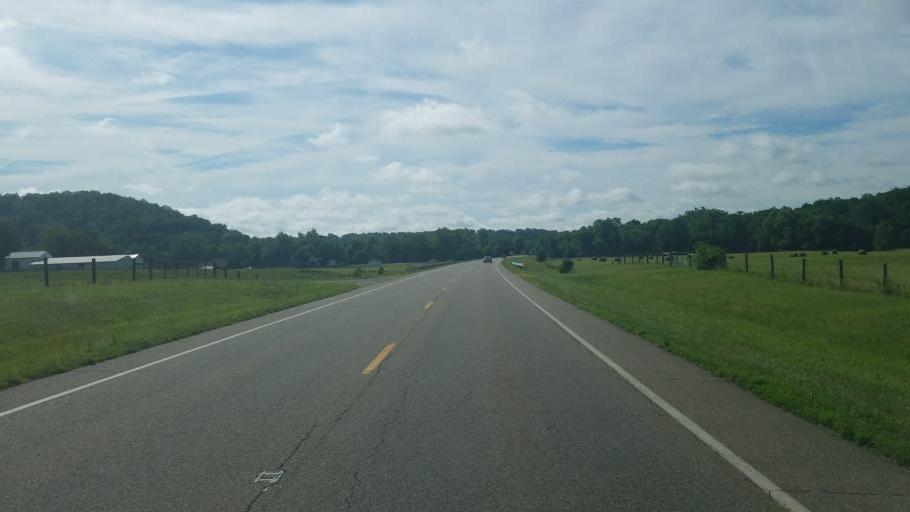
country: US
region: Ohio
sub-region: Gallia County
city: Gallipolis
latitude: 38.8776
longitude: -82.3610
